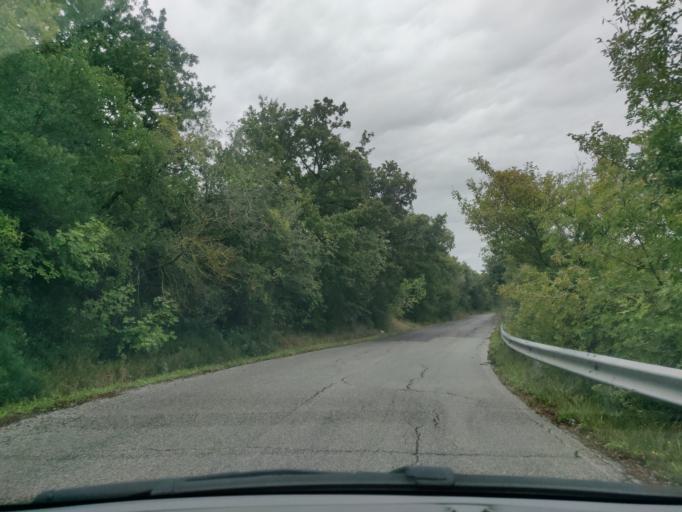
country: IT
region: Latium
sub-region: Citta metropolitana di Roma Capitale
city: Allumiere
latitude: 42.1289
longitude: 11.8560
